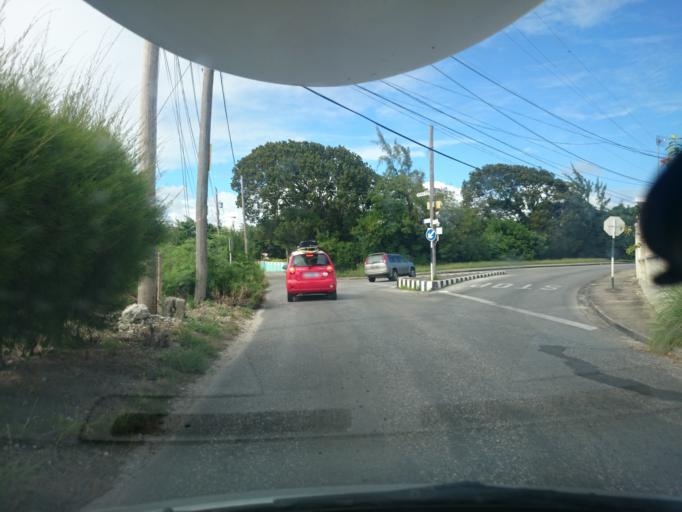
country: BB
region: Christ Church
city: Oistins
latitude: 13.0582
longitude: -59.5377
